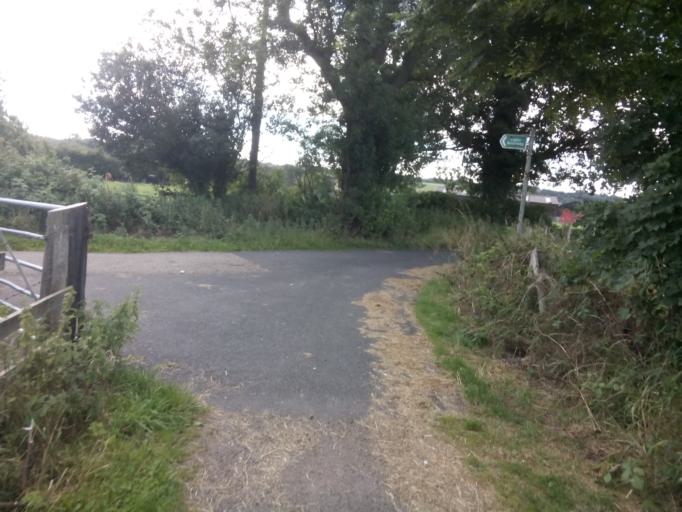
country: GB
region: England
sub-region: County Durham
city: Durham
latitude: 54.7937
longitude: -1.5620
